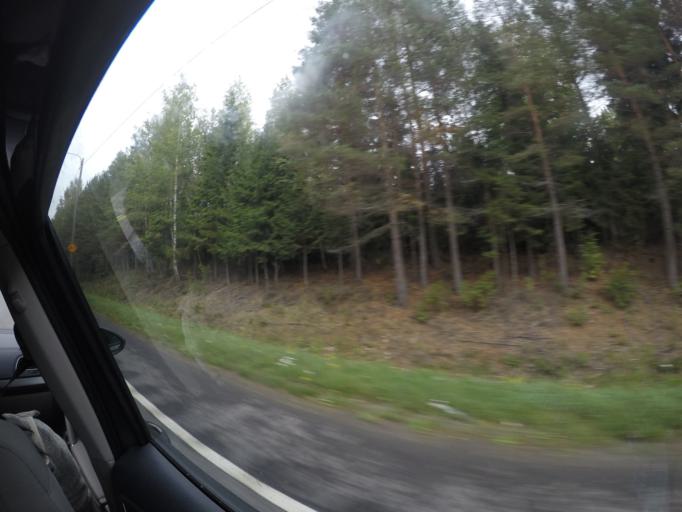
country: FI
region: Haeme
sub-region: Haemeenlinna
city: Parola
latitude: 61.1806
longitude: 24.4132
